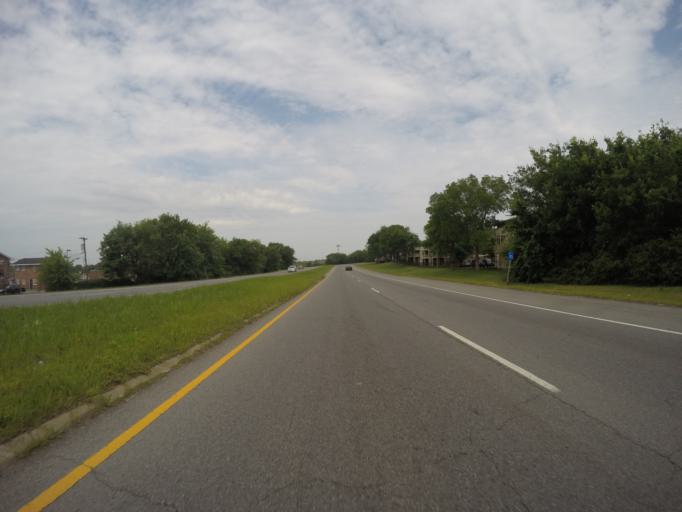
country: US
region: Tennessee
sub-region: Davidson County
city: Goodlettsville
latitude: 36.2639
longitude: -86.7047
